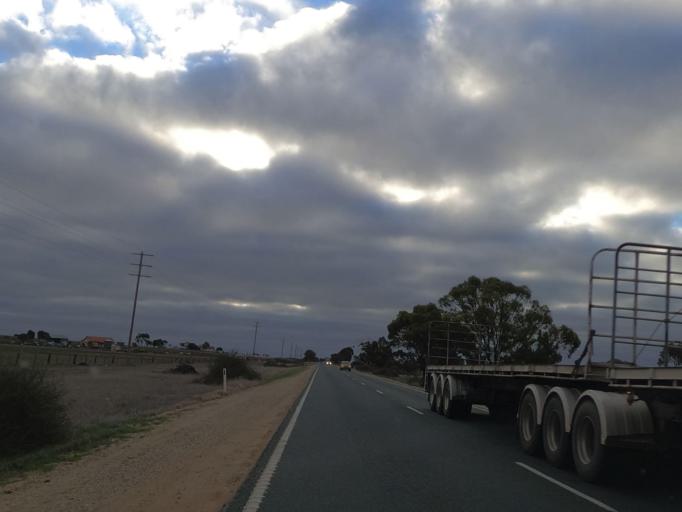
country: AU
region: Victoria
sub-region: Swan Hill
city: Swan Hill
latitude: -35.6445
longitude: 143.8330
